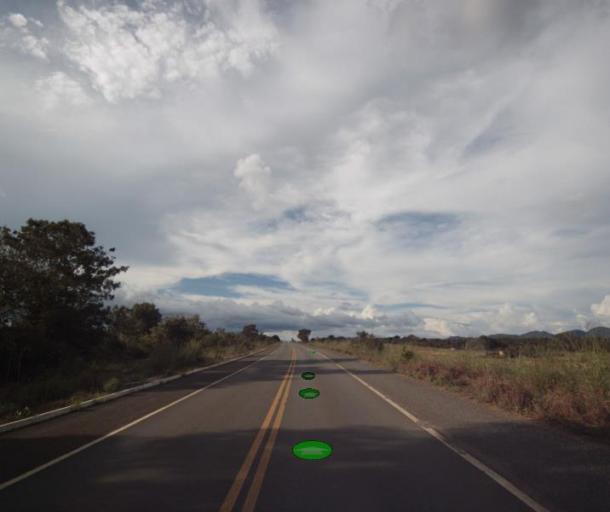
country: BR
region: Goias
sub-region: Niquelandia
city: Niquelandia
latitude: -14.7202
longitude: -48.6080
